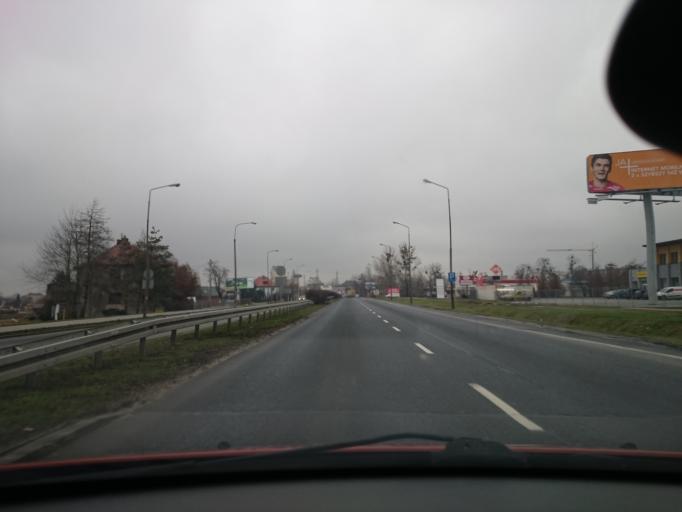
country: PL
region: Opole Voivodeship
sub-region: Powiat opolski
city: Chmielowice
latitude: 50.6788
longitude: 17.8825
